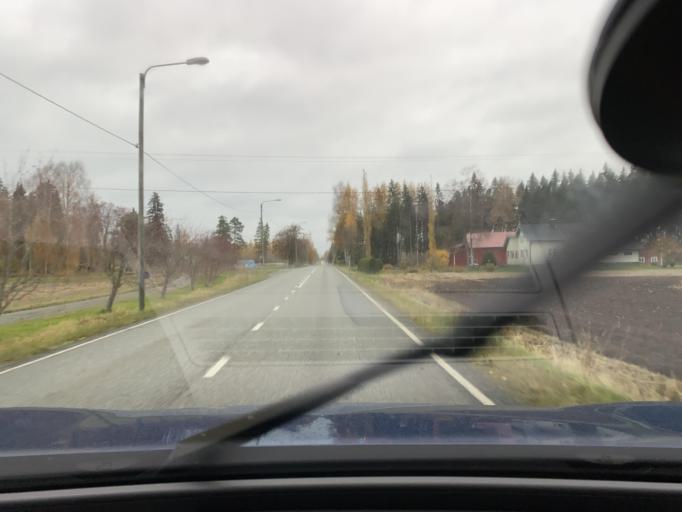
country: FI
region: Satakunta
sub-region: Pori
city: Vampula
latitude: 61.0716
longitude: 22.5269
